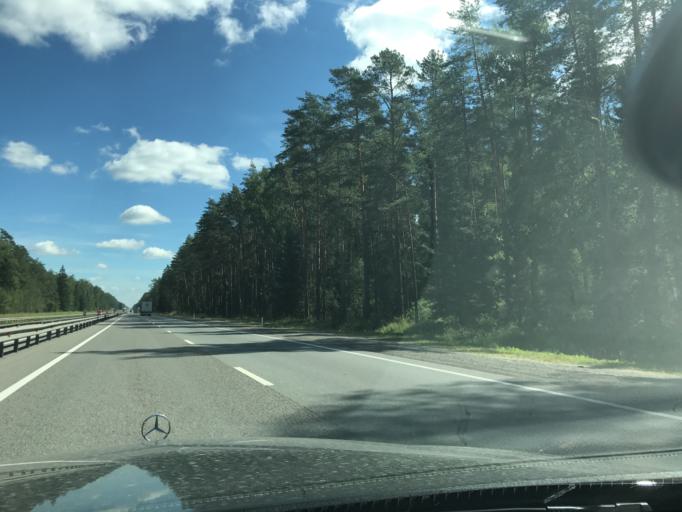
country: RU
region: Vladimir
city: Krasnyy Oktyabr'
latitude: 56.2215
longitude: 41.5308
